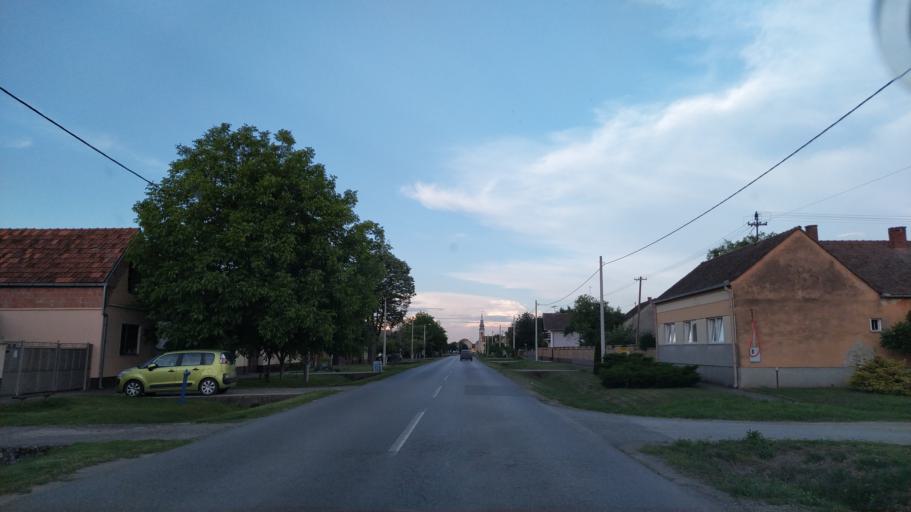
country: HR
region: Osjecko-Baranjska
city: Gorjani
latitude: 45.4609
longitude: 18.3168
